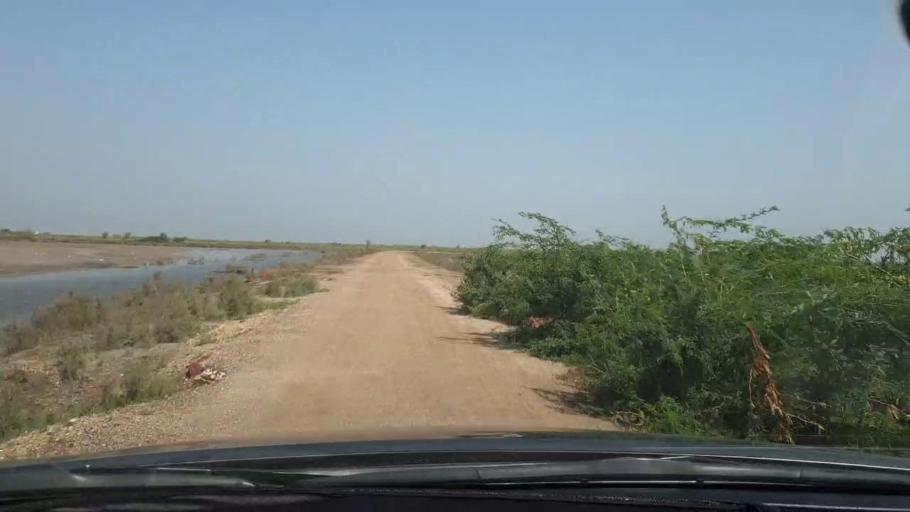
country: PK
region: Sindh
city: Tando Bago
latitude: 24.7898
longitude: 69.0787
